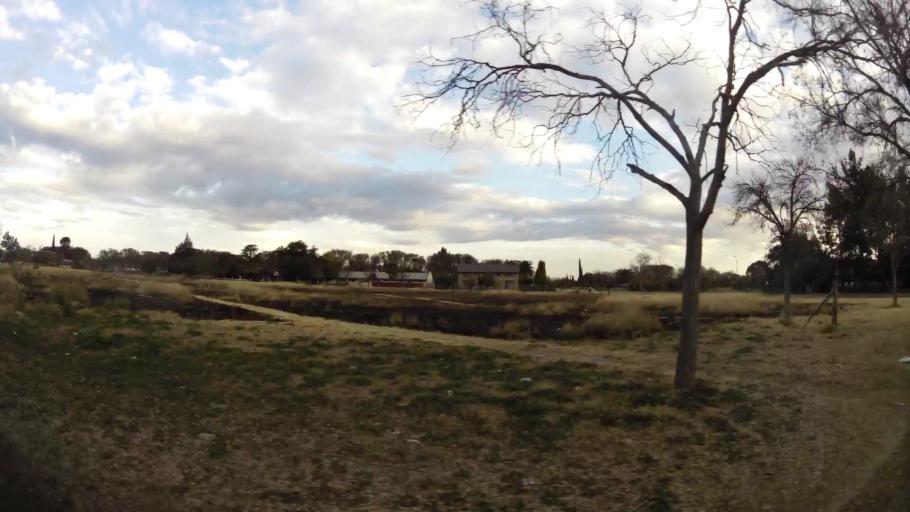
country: ZA
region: Orange Free State
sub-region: Lejweleputswa District Municipality
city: Welkom
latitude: -27.9780
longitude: 26.7120
